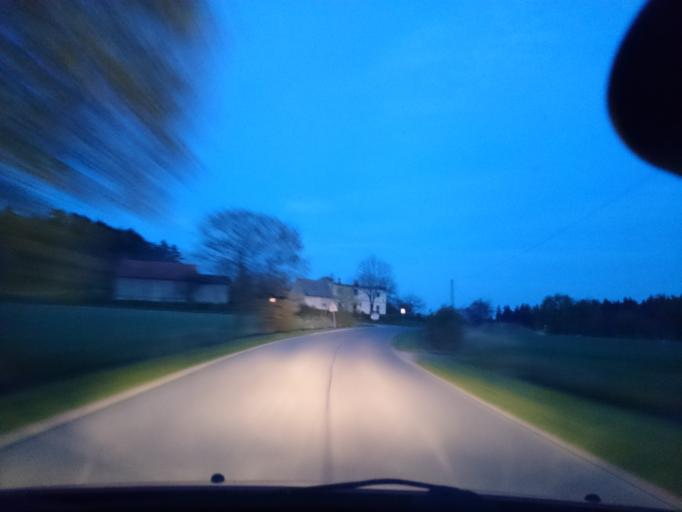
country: PL
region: Lower Silesian Voivodeship
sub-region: Powiat zabkowicki
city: Budzow
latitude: 50.5563
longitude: 16.7047
